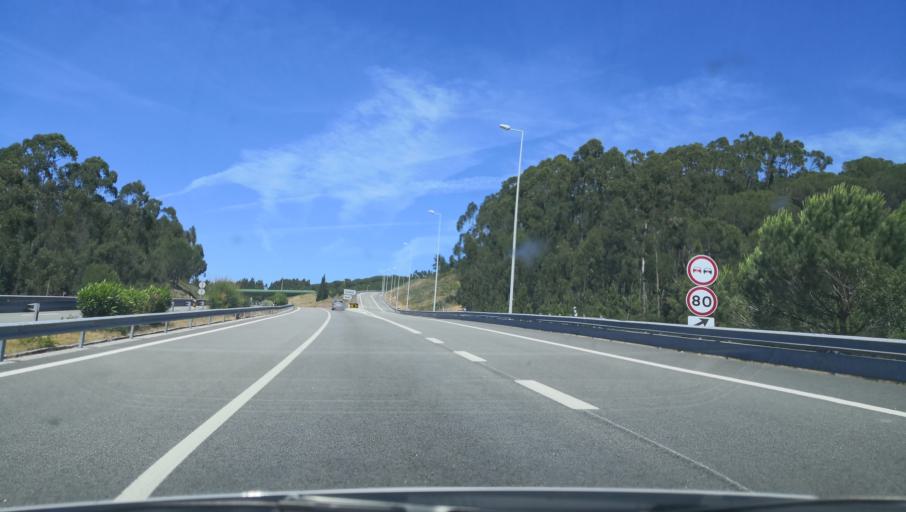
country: PT
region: Coimbra
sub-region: Montemor-O-Velho
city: Montemor-o-Velho
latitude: 40.1995
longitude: -8.6781
